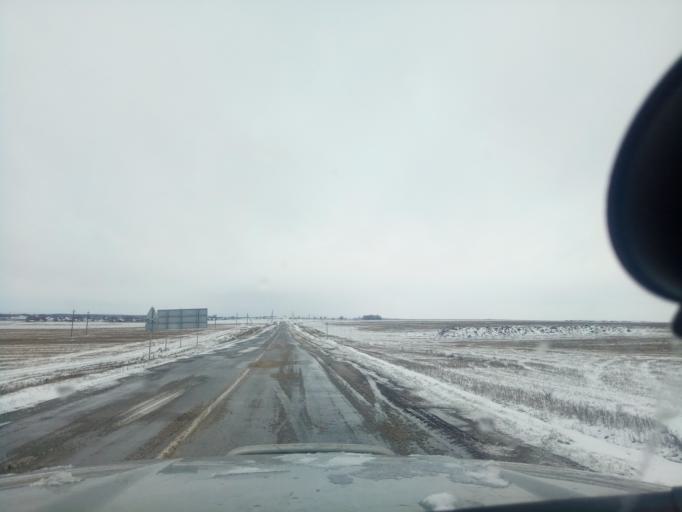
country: BY
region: Minsk
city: Klyetsk
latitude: 53.0315
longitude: 26.7244
